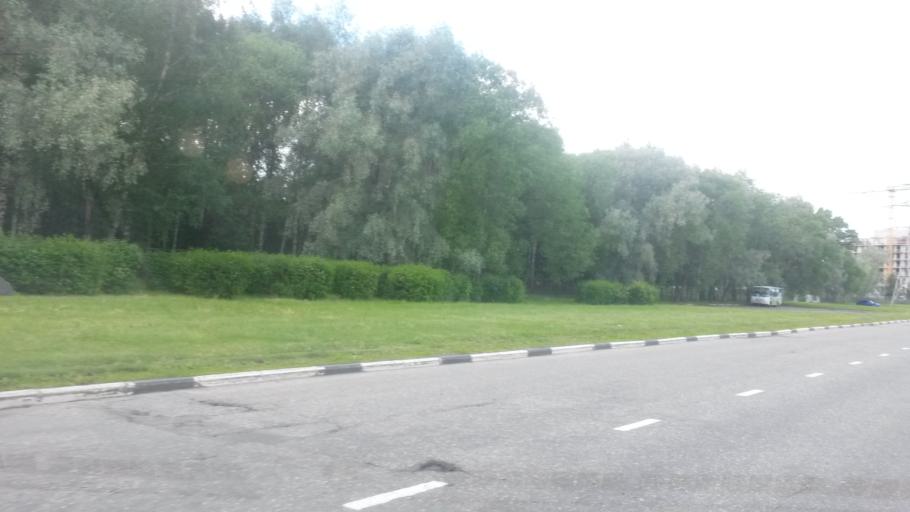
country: RU
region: Jaroslavl
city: Yaroslavl
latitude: 57.5864
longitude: 39.8529
